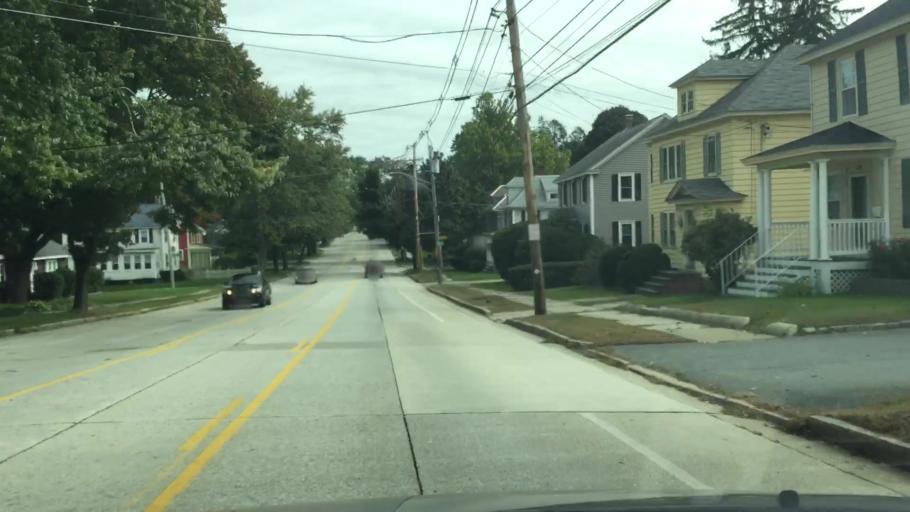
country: US
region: Massachusetts
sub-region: Middlesex County
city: Lowell
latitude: 42.6423
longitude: -71.2927
